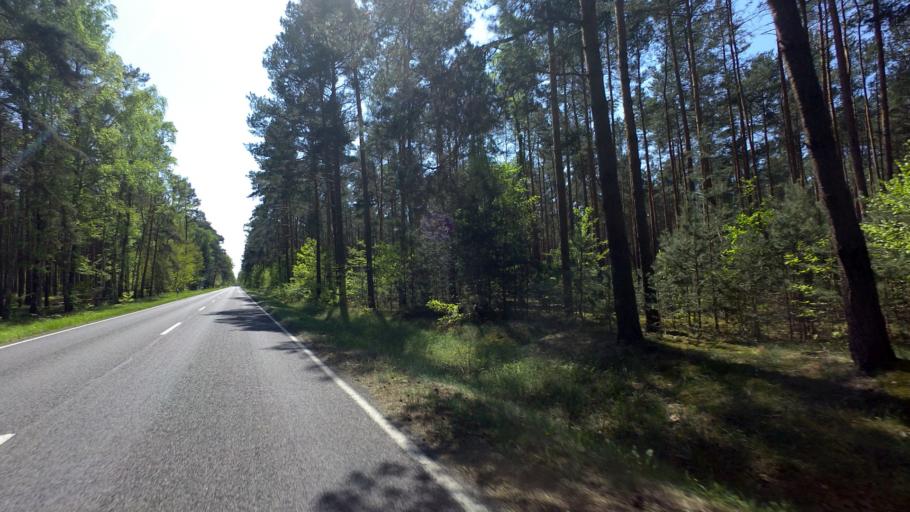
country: DE
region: Brandenburg
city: Gross Koris
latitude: 52.2036
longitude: 13.6923
